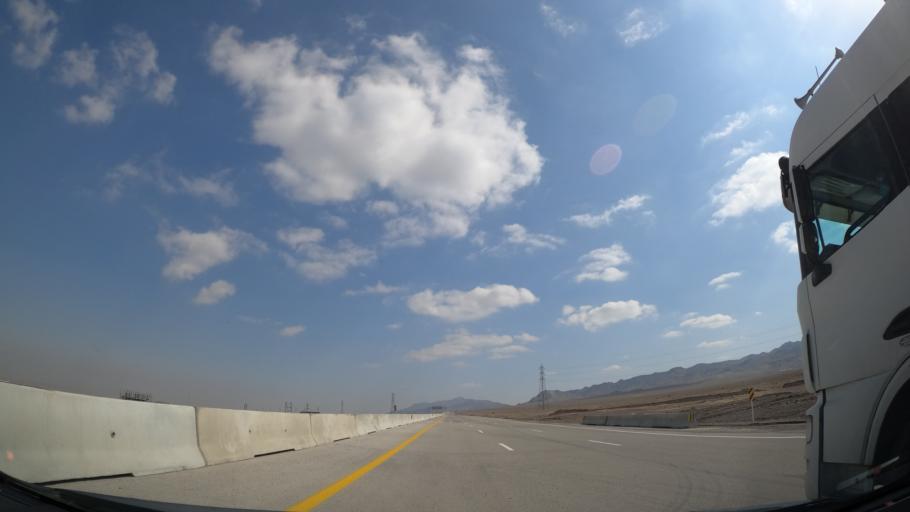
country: IR
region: Alborz
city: Eshtehard
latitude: 35.7170
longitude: 50.5768
